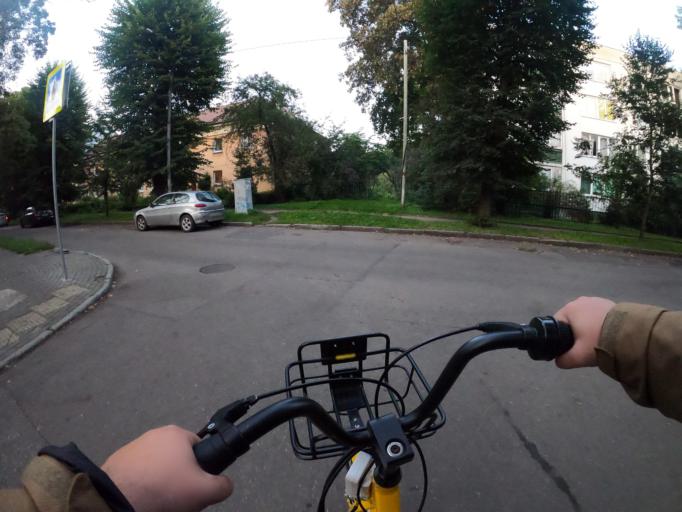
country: RU
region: Kaliningrad
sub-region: Gorod Kaliningrad
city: Kaliningrad
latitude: 54.7234
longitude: 20.4768
